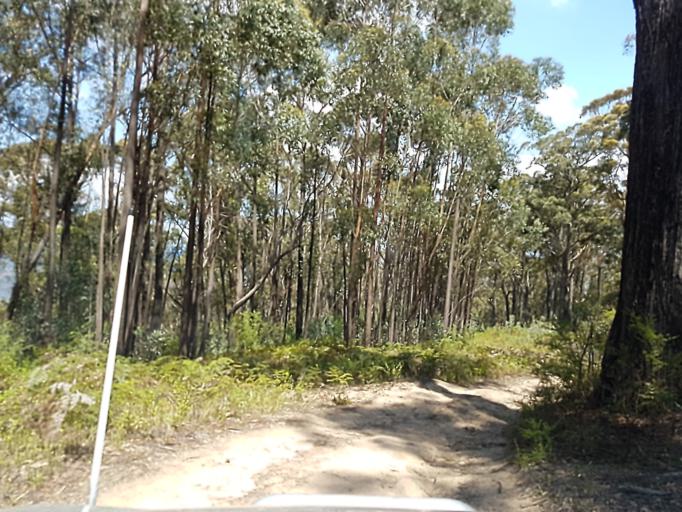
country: AU
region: Victoria
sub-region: East Gippsland
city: Lakes Entrance
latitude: -37.3995
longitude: 148.2984
